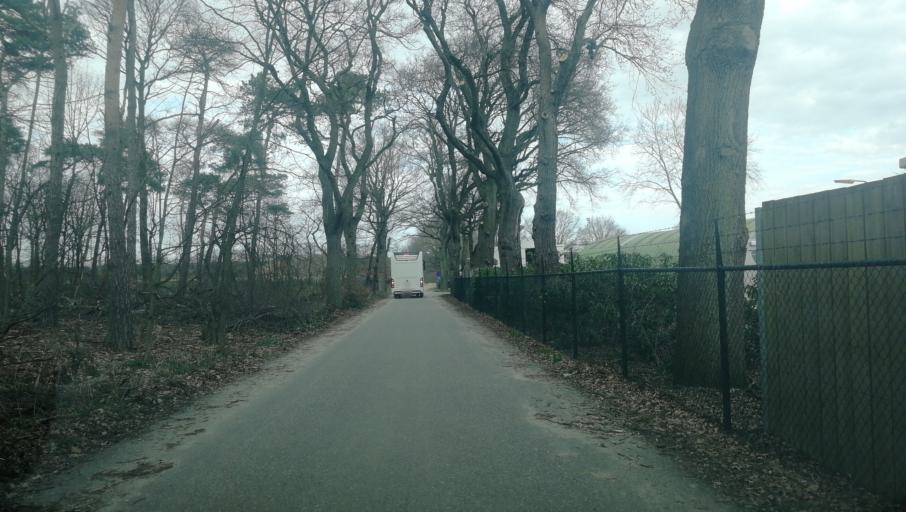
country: NL
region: Limburg
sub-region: Gemeente Venlo
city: Venlo
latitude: 51.3920
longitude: 6.1486
